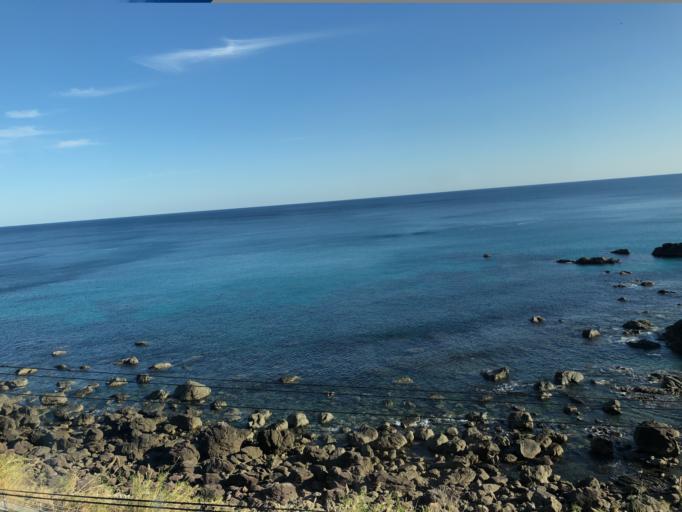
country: JP
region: Kochi
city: Nakamura
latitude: 33.0610
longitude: 133.1020
